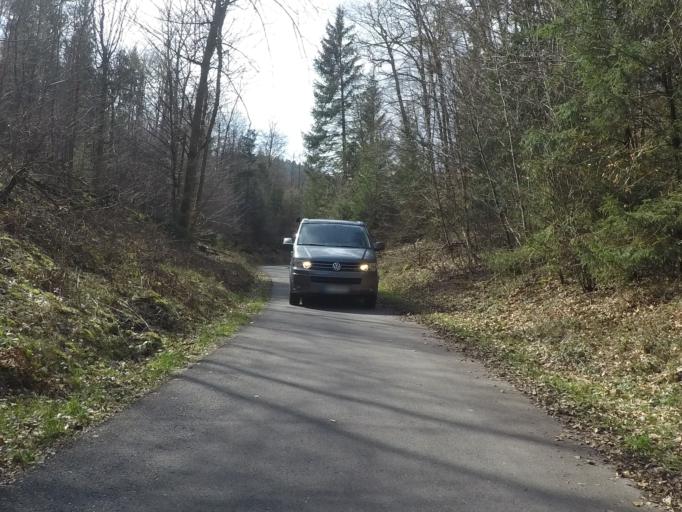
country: DE
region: Rheinland-Pfalz
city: Munchweiler an der Rodalbe
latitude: 49.2111
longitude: 7.7261
